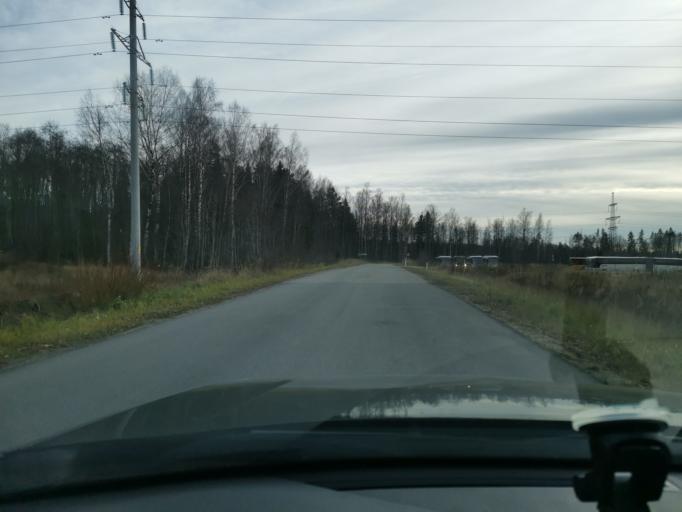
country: EE
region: Ida-Virumaa
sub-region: Sillamaee linn
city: Sillamae
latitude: 59.2717
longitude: 27.9129
